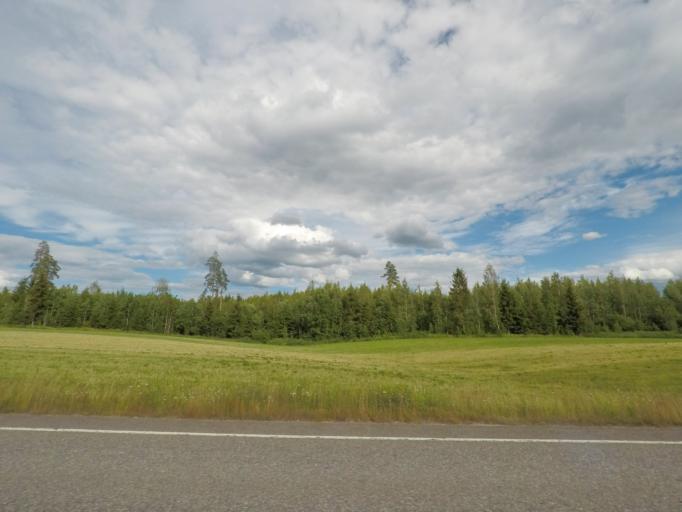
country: FI
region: Paijanne Tavastia
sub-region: Lahti
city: Hollola
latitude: 60.8274
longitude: 25.4889
